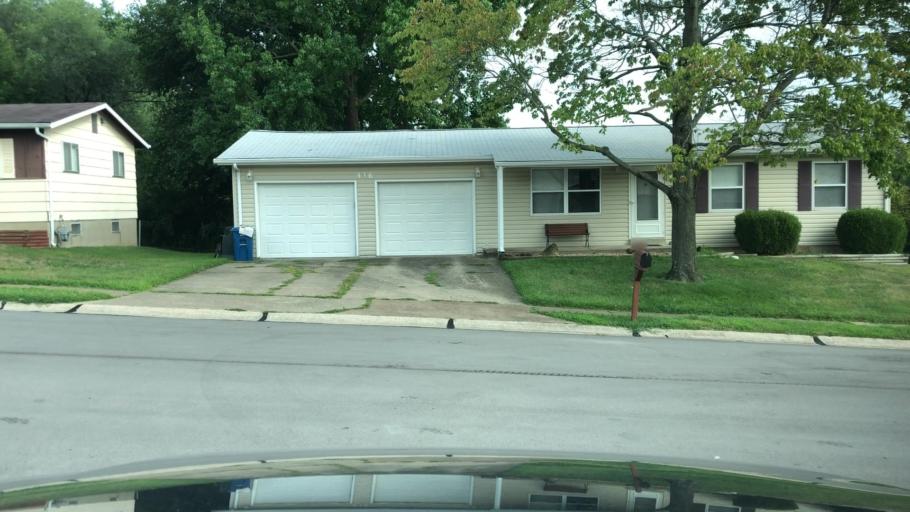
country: US
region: Missouri
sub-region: Saint Charles County
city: Saint Charles
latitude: 38.8114
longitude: -90.5086
